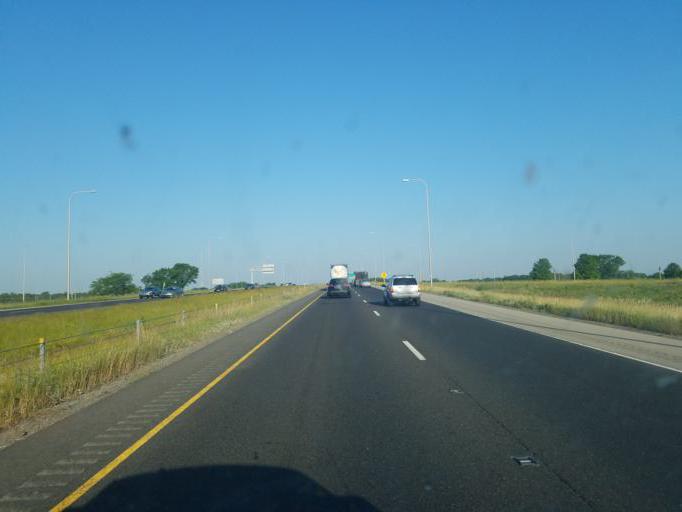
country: US
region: Illinois
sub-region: Will County
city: Shorewood
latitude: 41.4865
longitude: -88.1936
